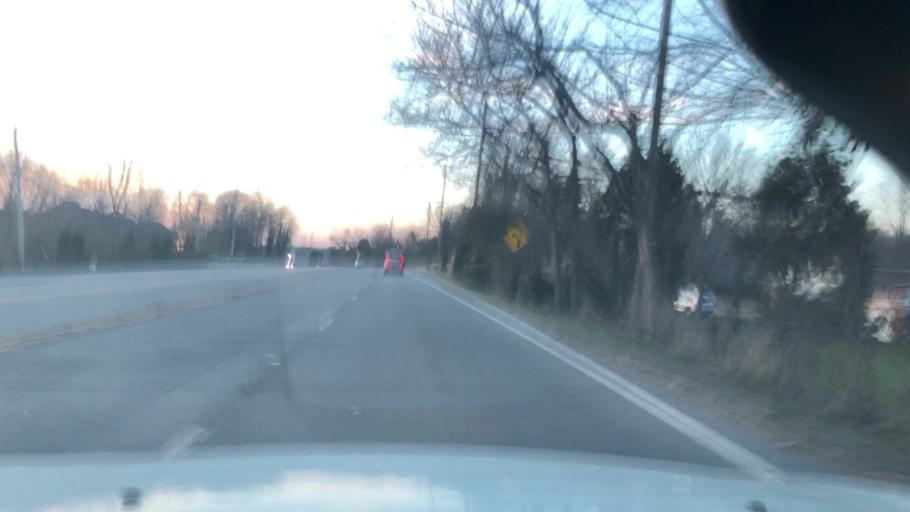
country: US
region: Kentucky
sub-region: Jefferson County
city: Anchorage
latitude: 38.2355
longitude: -85.4598
